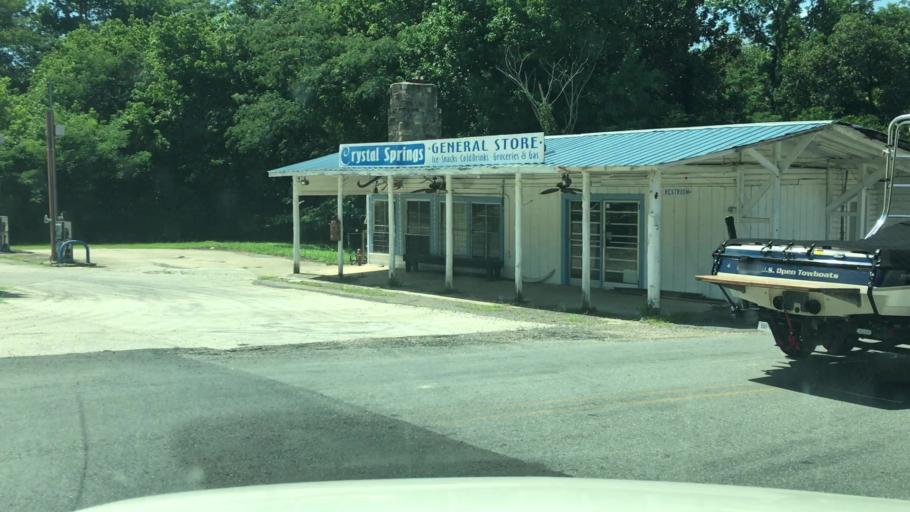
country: US
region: Arkansas
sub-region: Garland County
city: Rockwell
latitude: 34.5220
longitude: -93.3360
